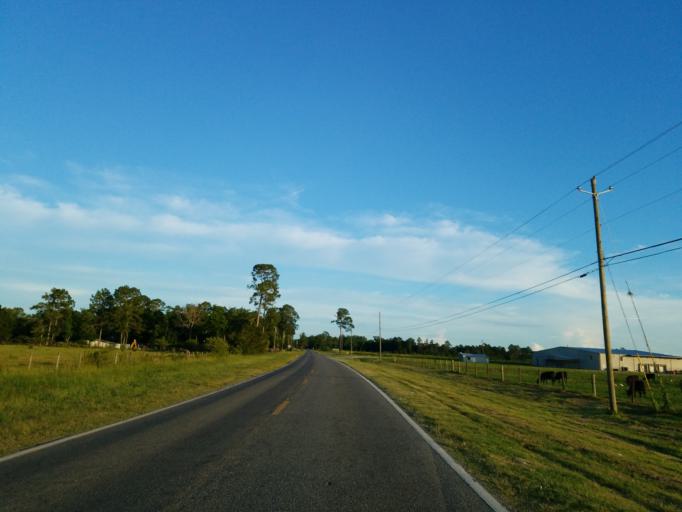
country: US
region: Georgia
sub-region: Cook County
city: Sparks
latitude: 31.1895
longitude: -83.4464
